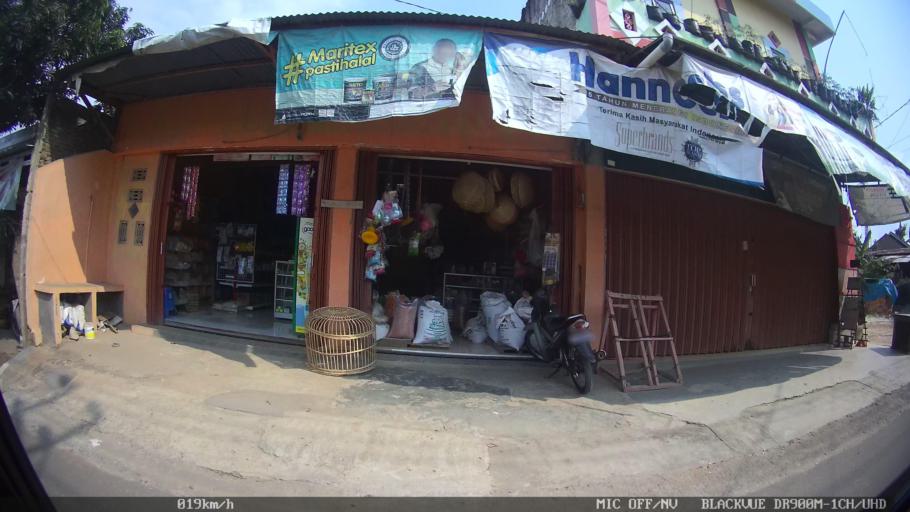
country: ID
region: Lampung
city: Natar
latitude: -5.3469
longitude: 105.2227
